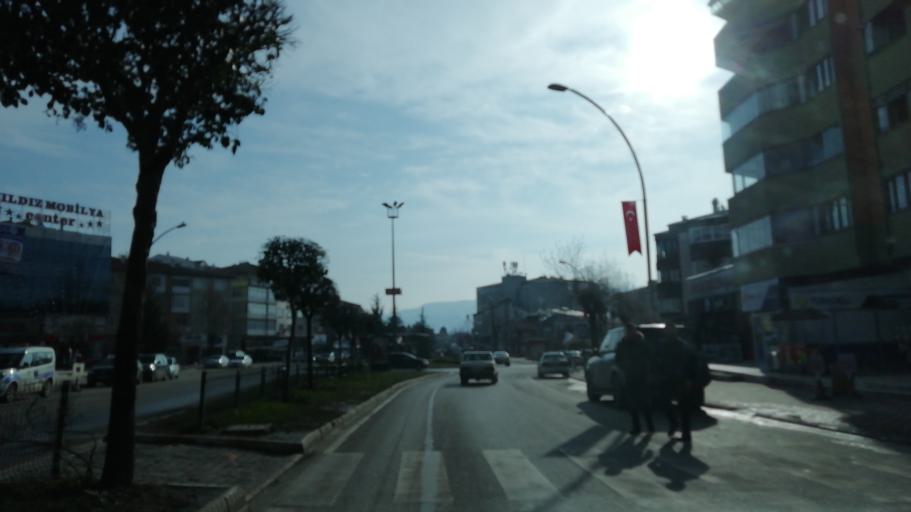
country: TR
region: Karabuk
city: Safranbolu
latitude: 41.2514
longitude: 32.6810
